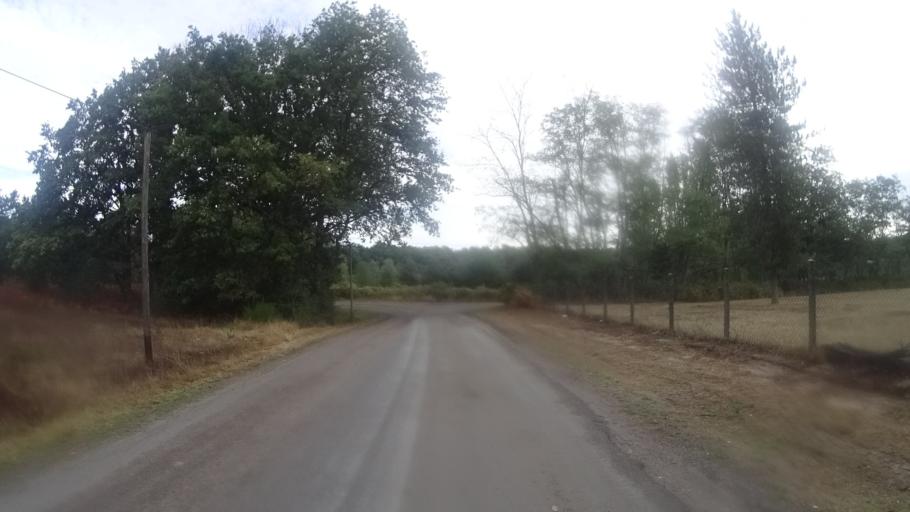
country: FR
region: Centre
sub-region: Departement du Loiret
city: Fay-aux-Loges
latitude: 47.9325
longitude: 2.1978
